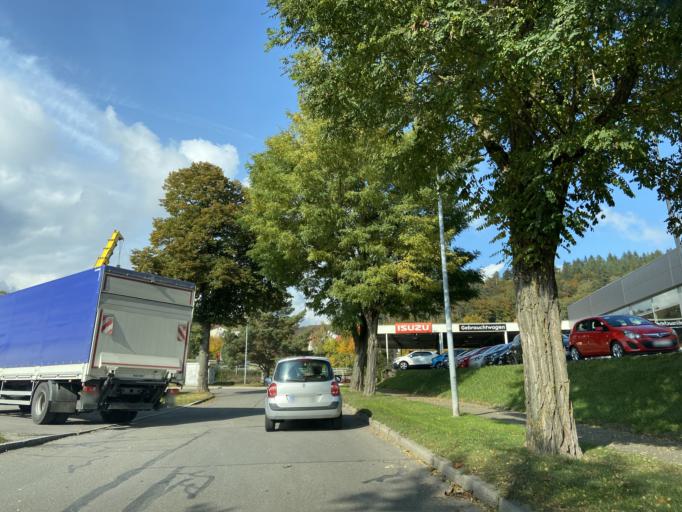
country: DE
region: Baden-Wuerttemberg
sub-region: Tuebingen Region
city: Sigmaringen
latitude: 48.0893
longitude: 9.2082
